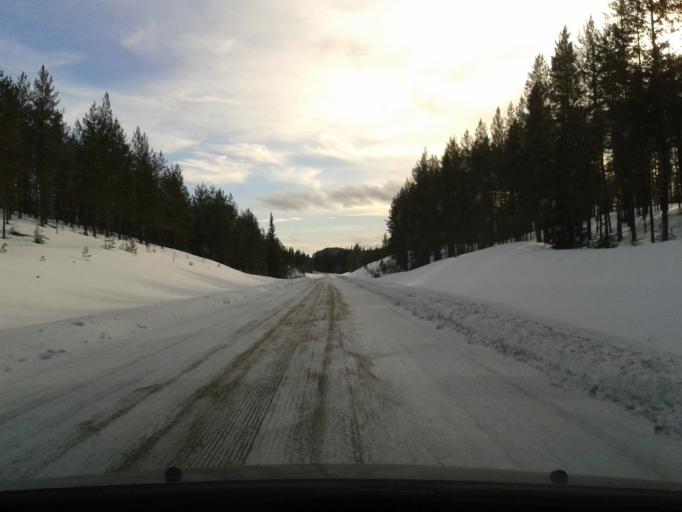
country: SE
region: Vaesterbotten
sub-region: Asele Kommun
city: Asele
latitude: 64.2901
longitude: 17.2600
